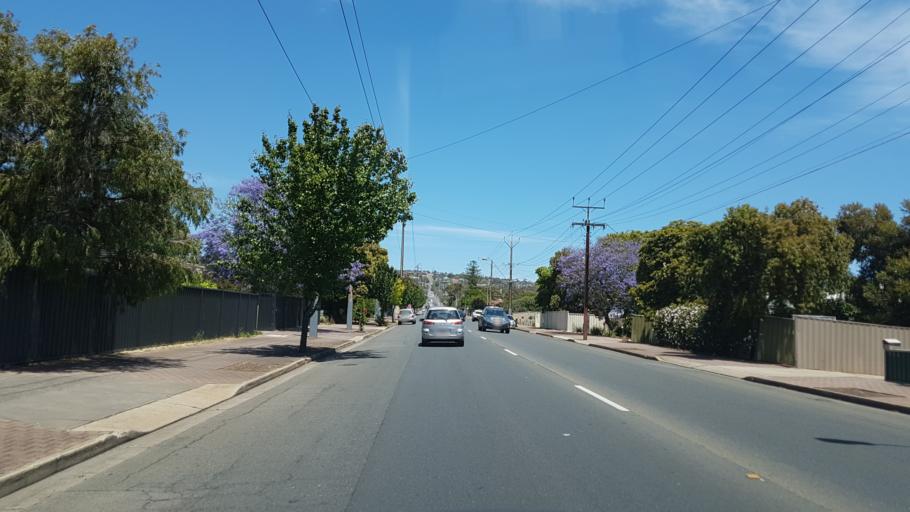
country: AU
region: South Australia
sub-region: Marion
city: Sturt
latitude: -35.0209
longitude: 138.5414
